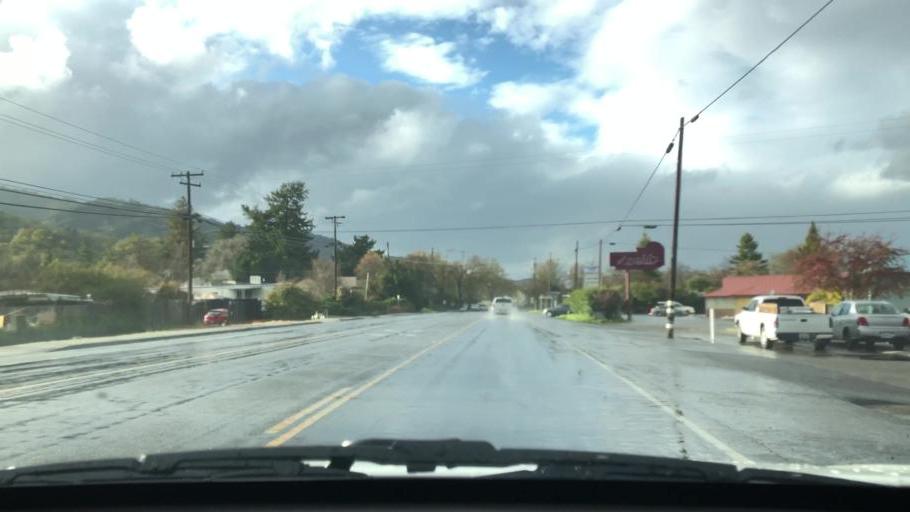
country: US
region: California
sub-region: Mendocino County
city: Ukiah
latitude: 39.1197
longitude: -123.2021
